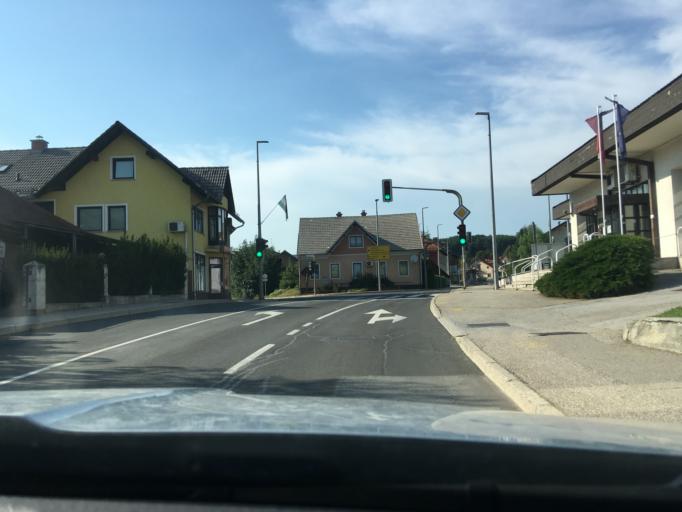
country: SI
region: Crnomelj
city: Crnomelj
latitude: 45.5745
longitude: 15.1902
